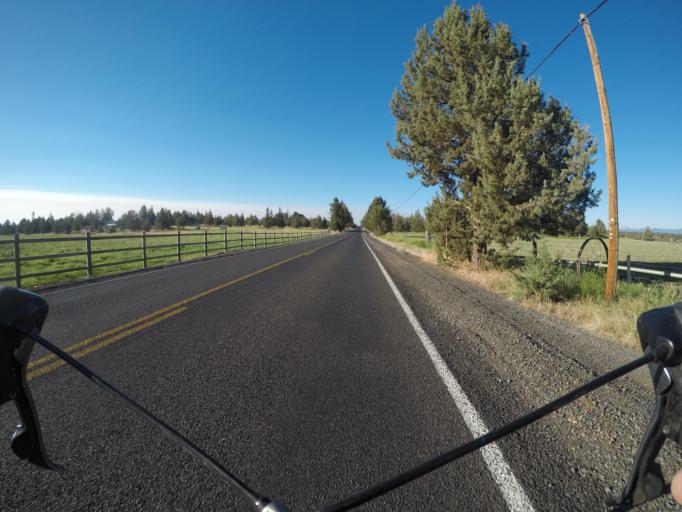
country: US
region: Oregon
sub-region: Deschutes County
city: Redmond
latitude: 44.2610
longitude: -121.2395
